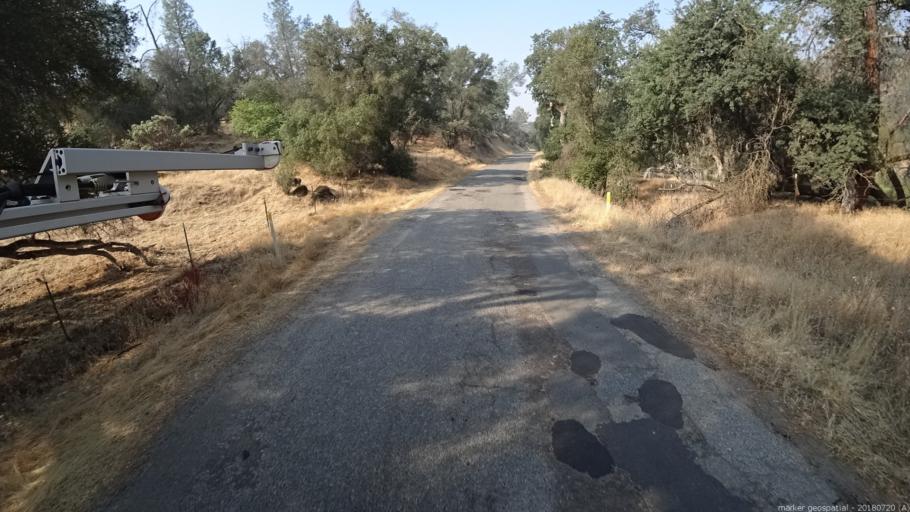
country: US
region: California
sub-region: Madera County
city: Yosemite Lakes
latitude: 37.2833
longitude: -119.8715
